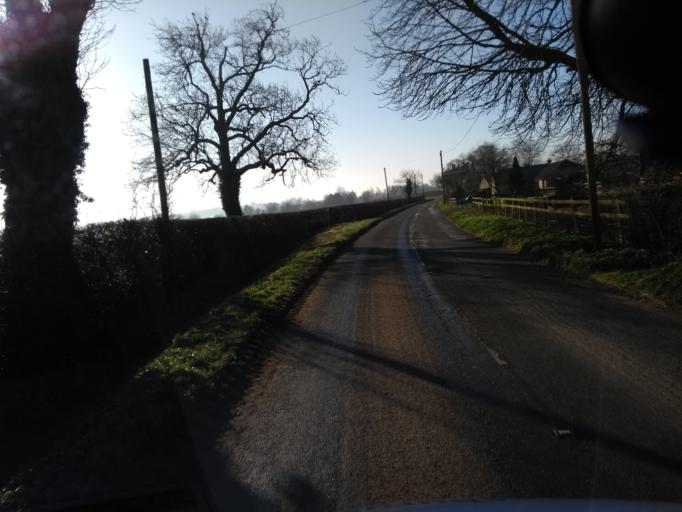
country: GB
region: England
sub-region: Somerset
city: Wincanton
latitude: 51.0777
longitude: -2.4121
